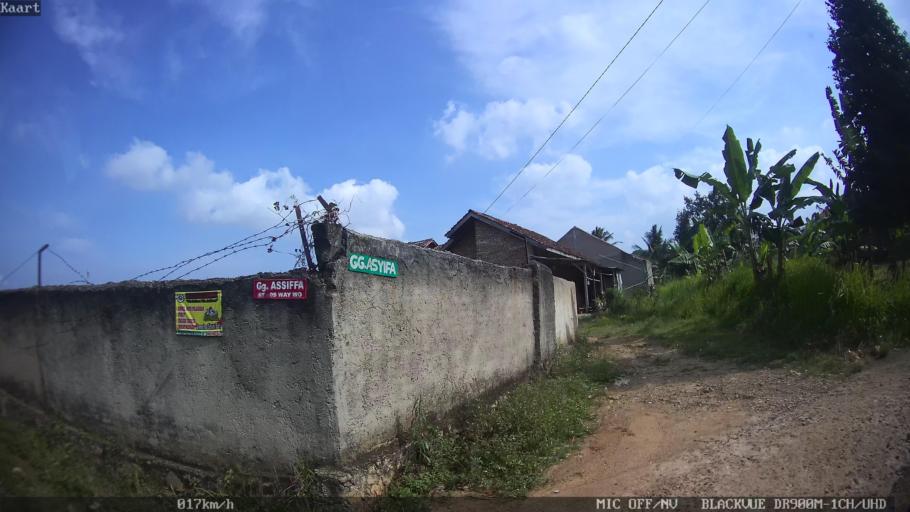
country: ID
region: Lampung
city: Kedaton
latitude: -5.3827
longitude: 105.2291
